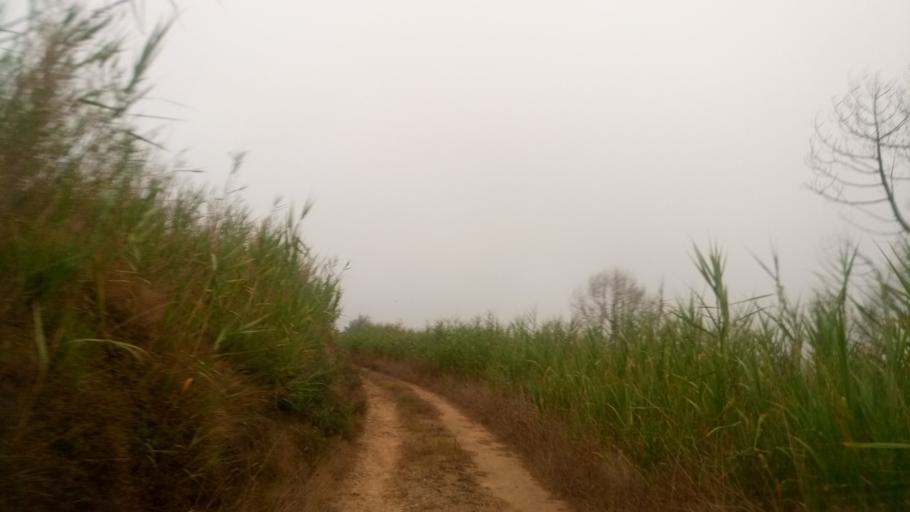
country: PT
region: Leiria
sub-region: Caldas da Rainha
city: Caldas da Rainha
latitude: 39.4662
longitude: -9.1965
